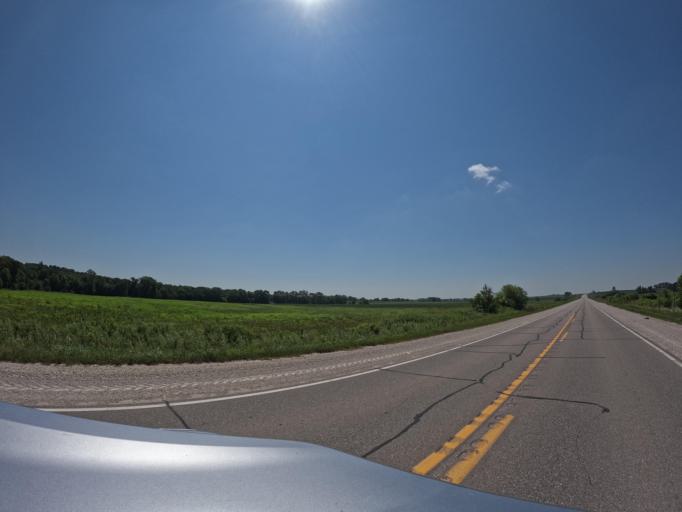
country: US
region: Iowa
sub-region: Keokuk County
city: Sigourney
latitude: 41.2994
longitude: -92.2047
